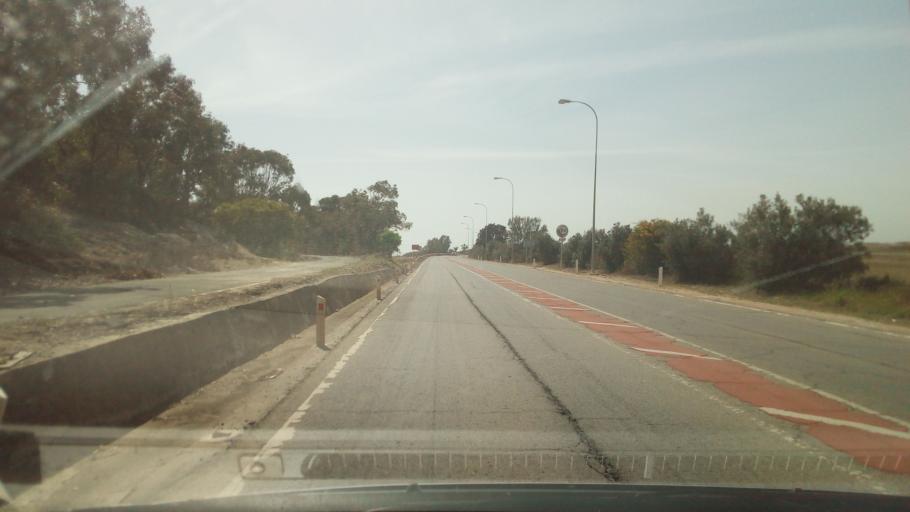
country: CY
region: Larnaka
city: Pyla
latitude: 34.9826
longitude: 33.7161
